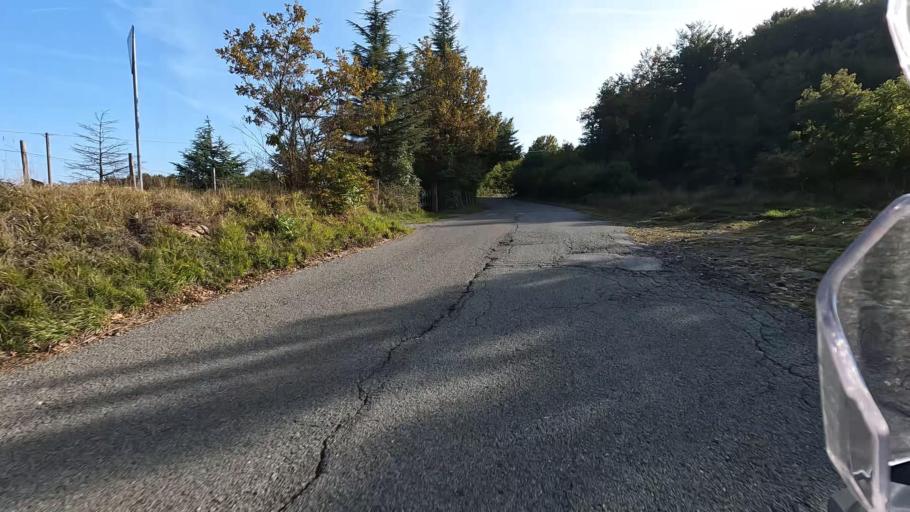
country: IT
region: Liguria
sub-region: Provincia di Savona
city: Urbe
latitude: 44.4718
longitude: 8.5613
